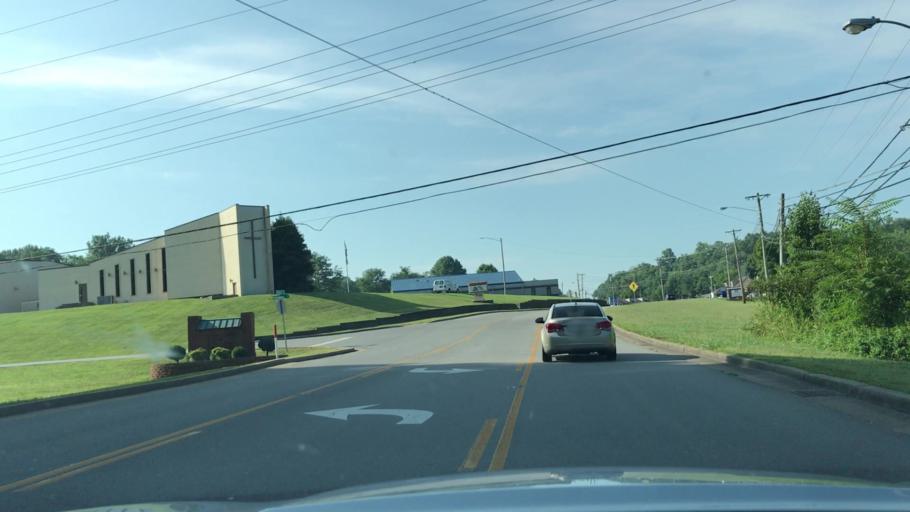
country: US
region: Kentucky
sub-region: Barren County
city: Glasgow
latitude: 37.0171
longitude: -85.9066
